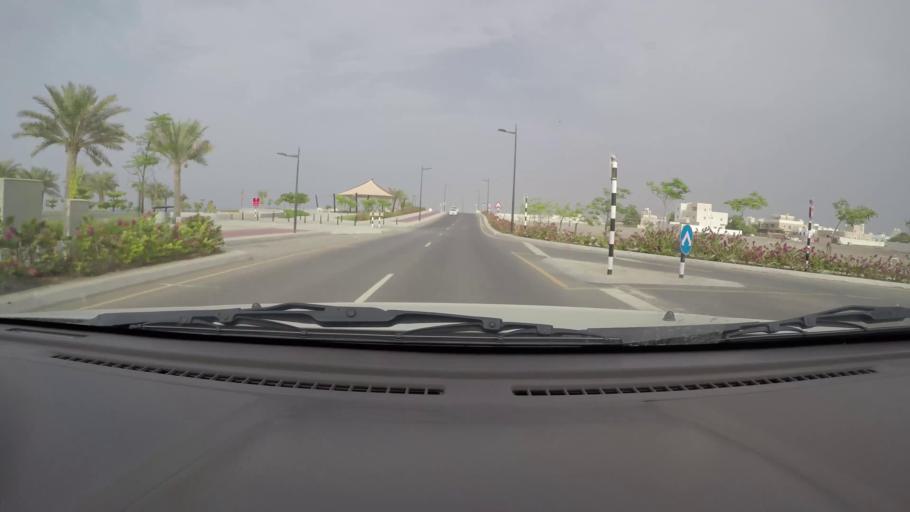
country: OM
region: Muhafazat Masqat
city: As Sib al Jadidah
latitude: 23.6933
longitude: 58.1625
